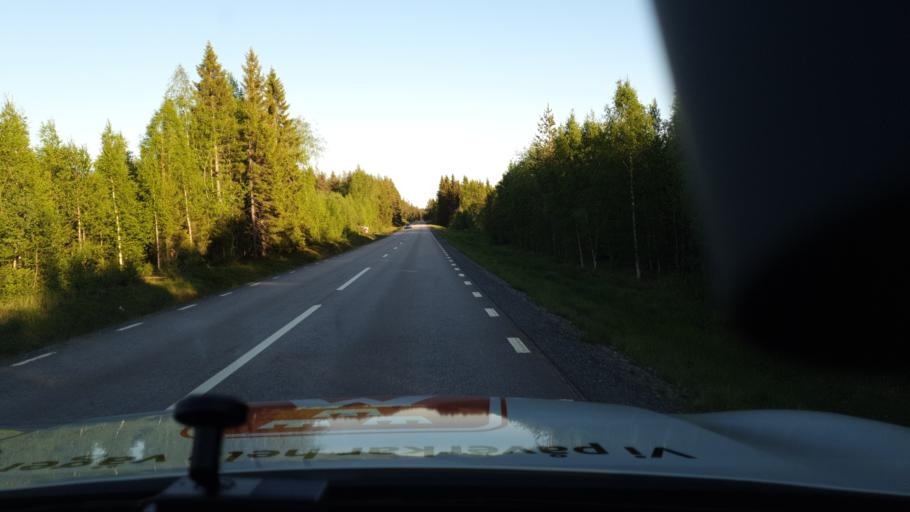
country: SE
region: Vaesterbotten
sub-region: Umea Kommun
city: Ersmark
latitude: 63.9550
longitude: 20.2947
